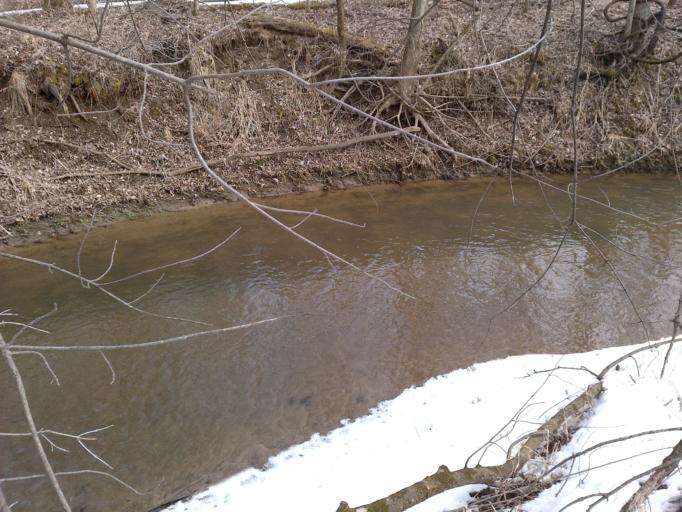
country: US
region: Minnesota
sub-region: Wabasha County
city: Lake City
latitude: 44.4515
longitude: -92.2989
